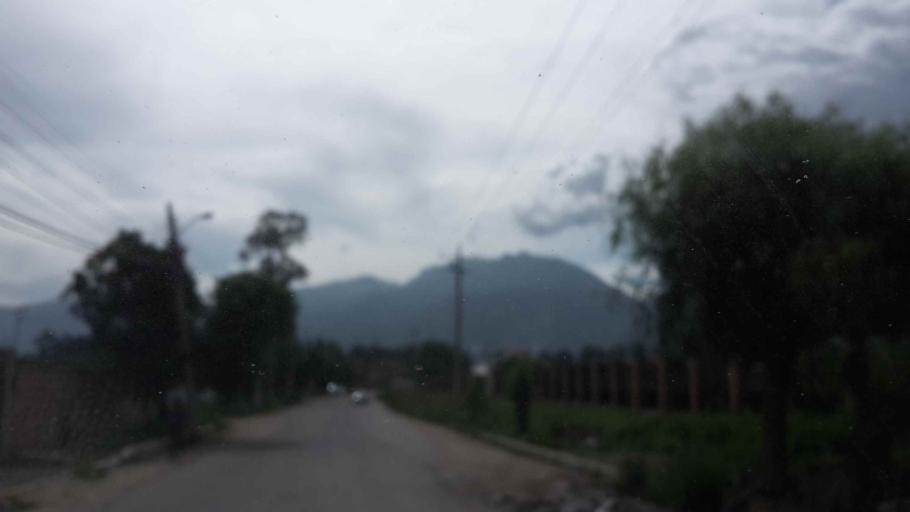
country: BO
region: Cochabamba
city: Cochabamba
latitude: -17.3358
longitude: -66.2314
